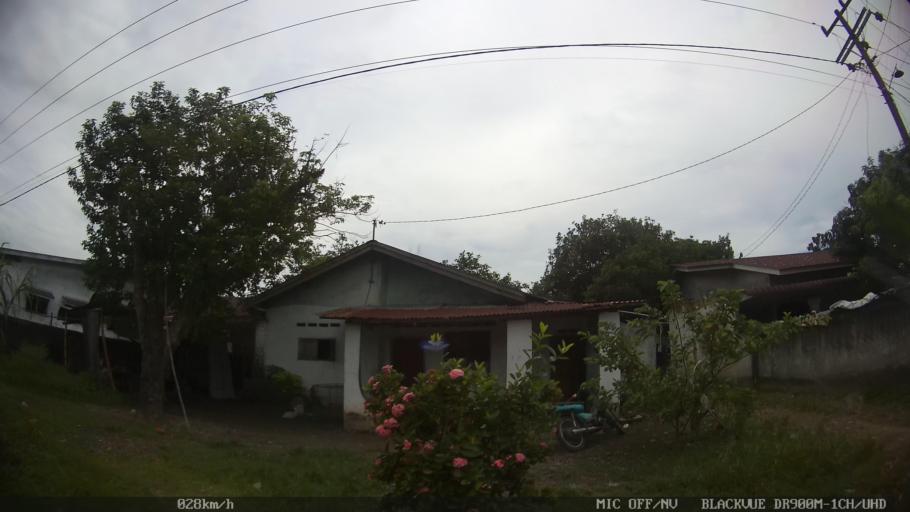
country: ID
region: North Sumatra
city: Sunggal
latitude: 3.6150
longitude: 98.6004
